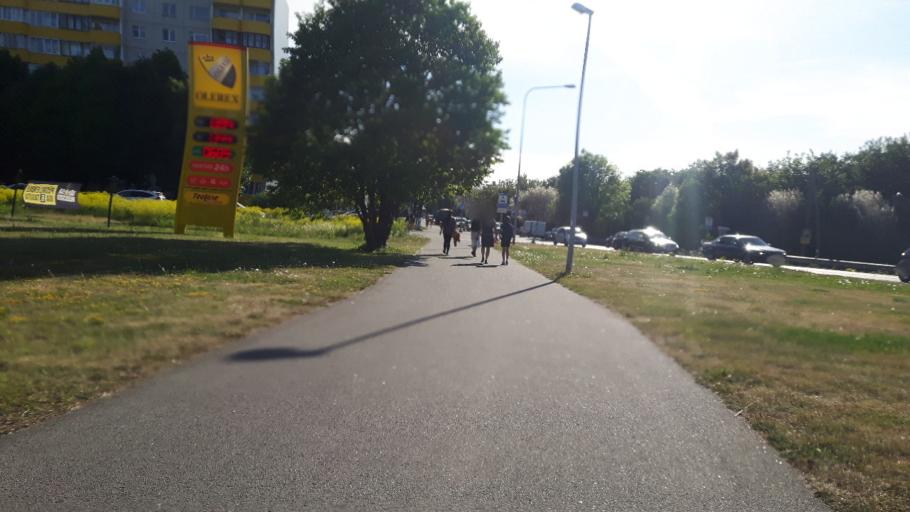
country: EE
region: Harju
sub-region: Tallinna linn
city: Kose
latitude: 59.4519
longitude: 24.8539
